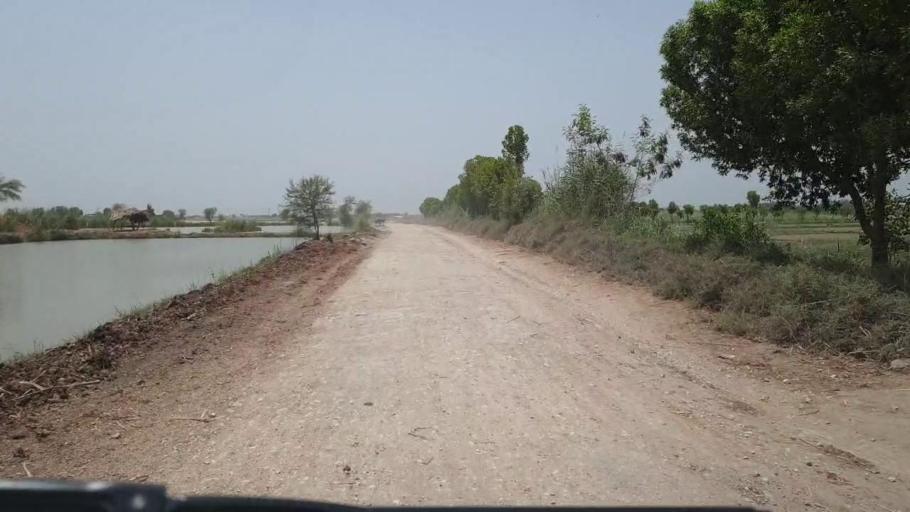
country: PK
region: Sindh
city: Daur
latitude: 26.4584
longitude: 68.1537
